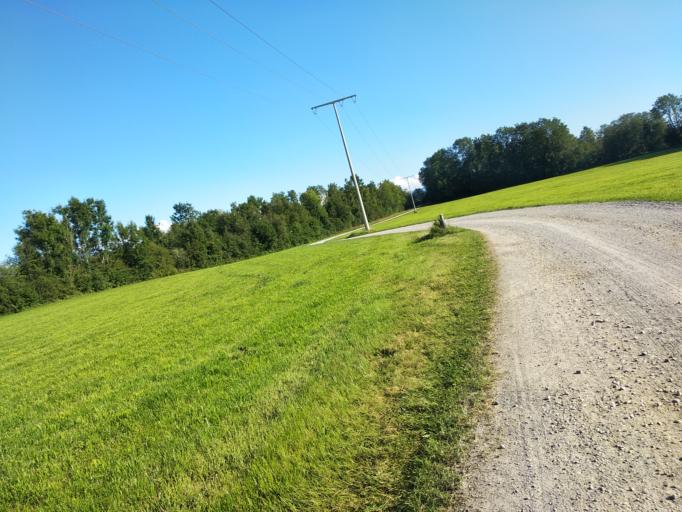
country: DE
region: Baden-Wuerttemberg
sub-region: Tuebingen Region
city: Leutkirch im Allgau
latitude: 47.7702
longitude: 10.0441
